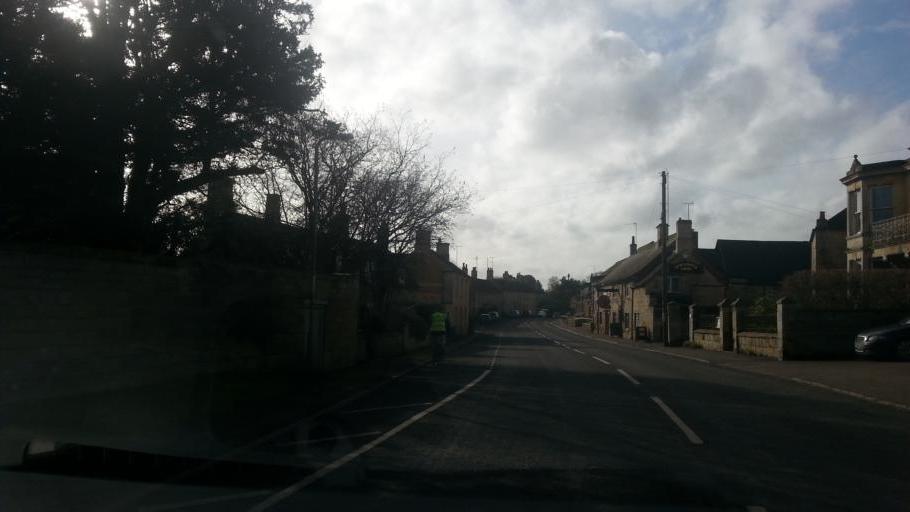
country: GB
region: England
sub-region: District of Rutland
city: Ketton
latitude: 52.6329
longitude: -0.5500
